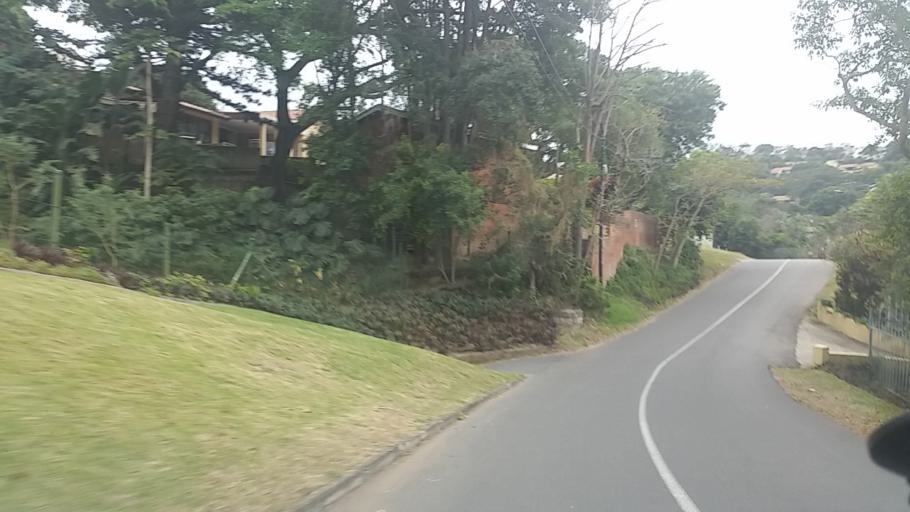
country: ZA
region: KwaZulu-Natal
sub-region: eThekwini Metropolitan Municipality
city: Berea
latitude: -29.8424
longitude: 30.9341
